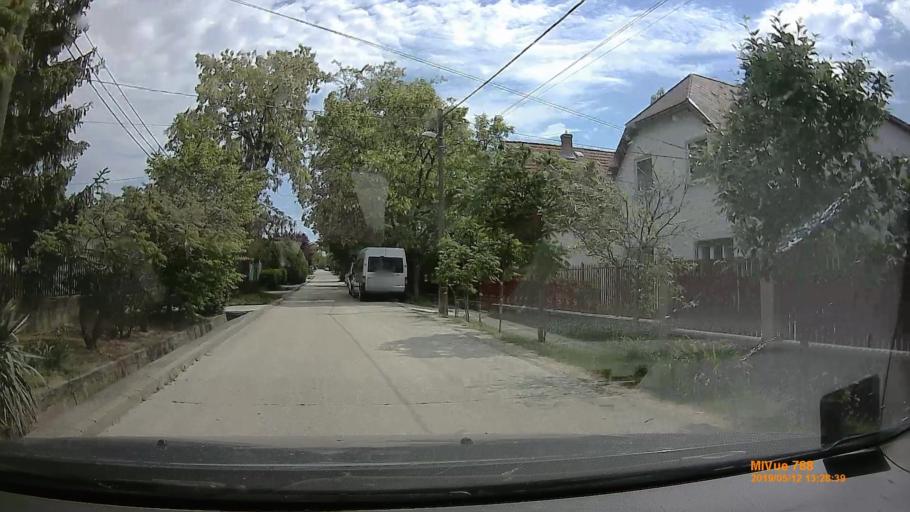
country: HU
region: Budapest
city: Budapest XVII. keruelet
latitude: 47.4805
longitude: 19.2948
